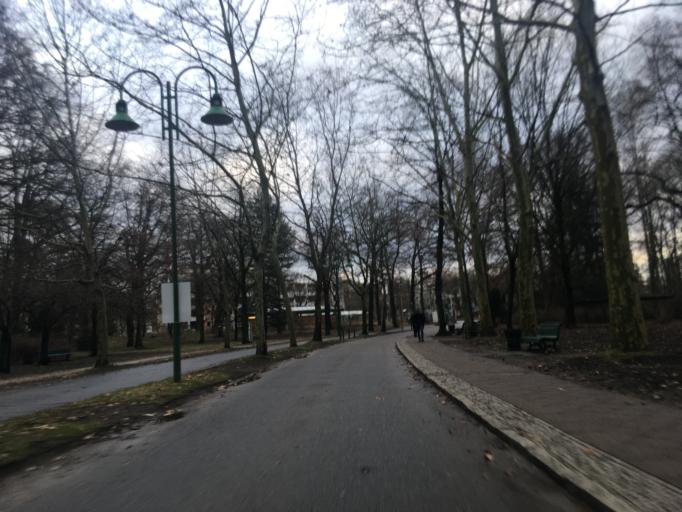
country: DE
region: Berlin
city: Reinickendorf
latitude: 52.5796
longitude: 13.3314
